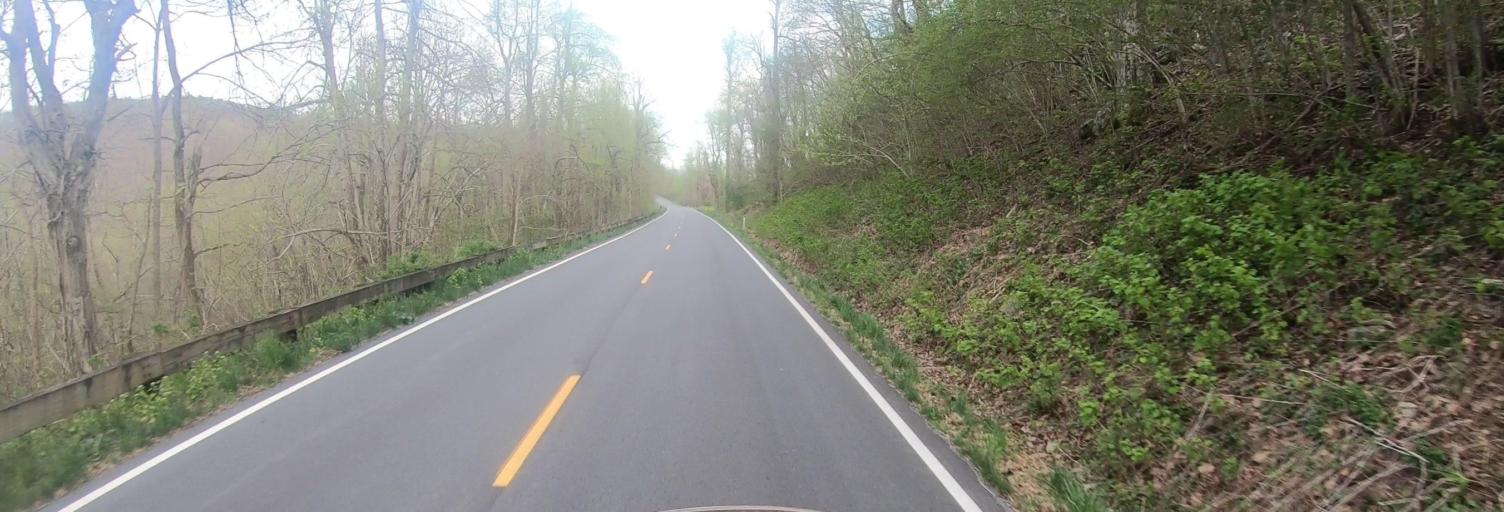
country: US
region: Virginia
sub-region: Augusta County
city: Dooms
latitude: 38.0608
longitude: -78.8195
